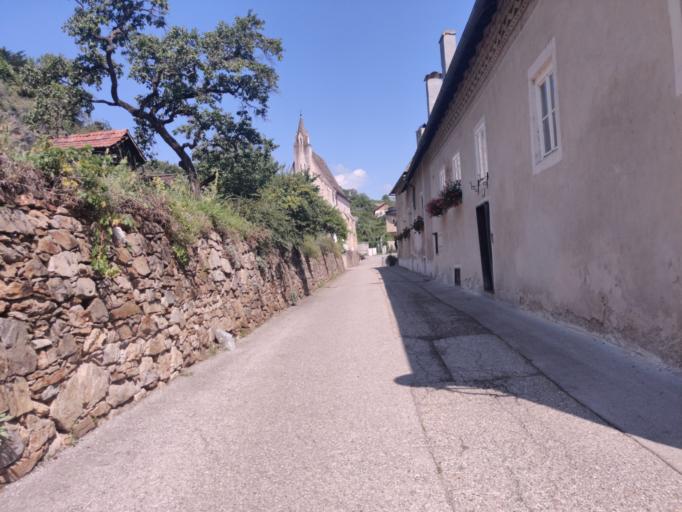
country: AT
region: Lower Austria
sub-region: Politischer Bezirk Krems
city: Weinzierl bei Krems
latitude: 48.3980
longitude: 15.5686
